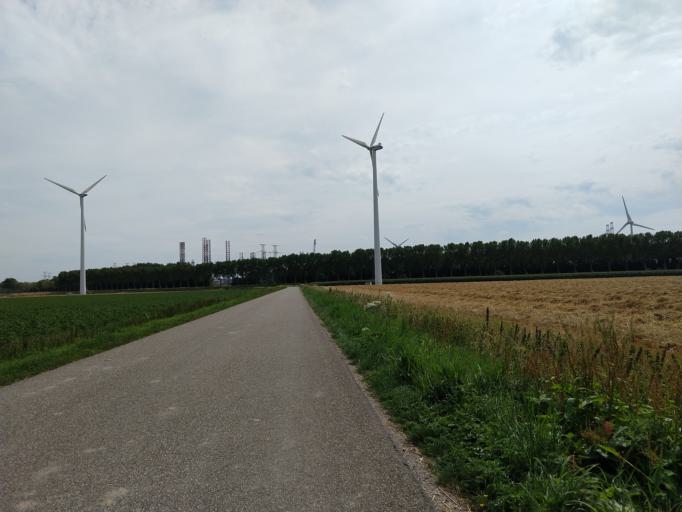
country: NL
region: Zeeland
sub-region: Gemeente Borsele
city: Borssele
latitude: 51.4844
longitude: 3.7122
